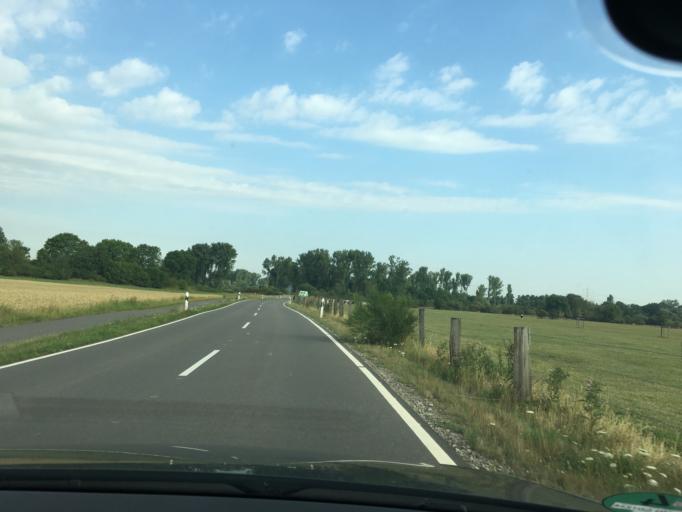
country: DE
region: North Rhine-Westphalia
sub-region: Regierungsbezirk Koln
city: Inden
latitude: 50.8922
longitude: 6.3737
